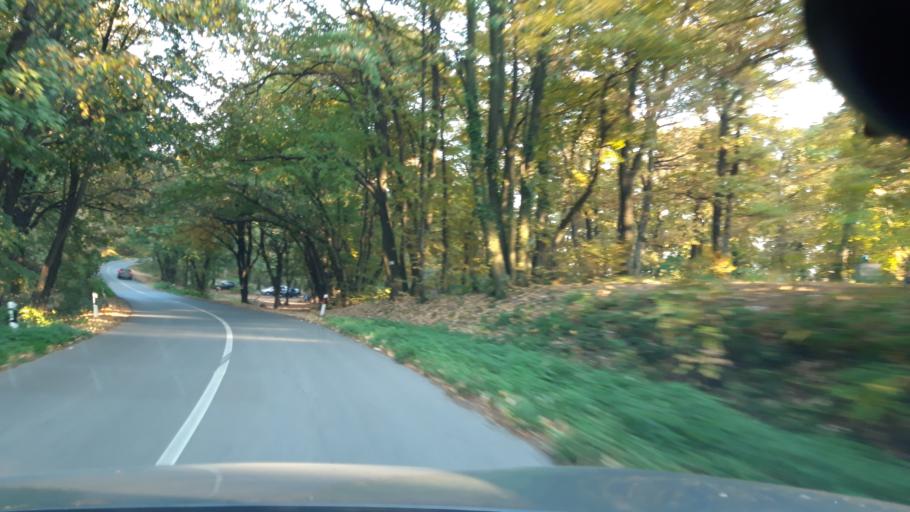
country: RS
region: Autonomna Pokrajina Vojvodina
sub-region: Sremski Okrug
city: Irig
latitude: 45.1543
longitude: 19.8449
